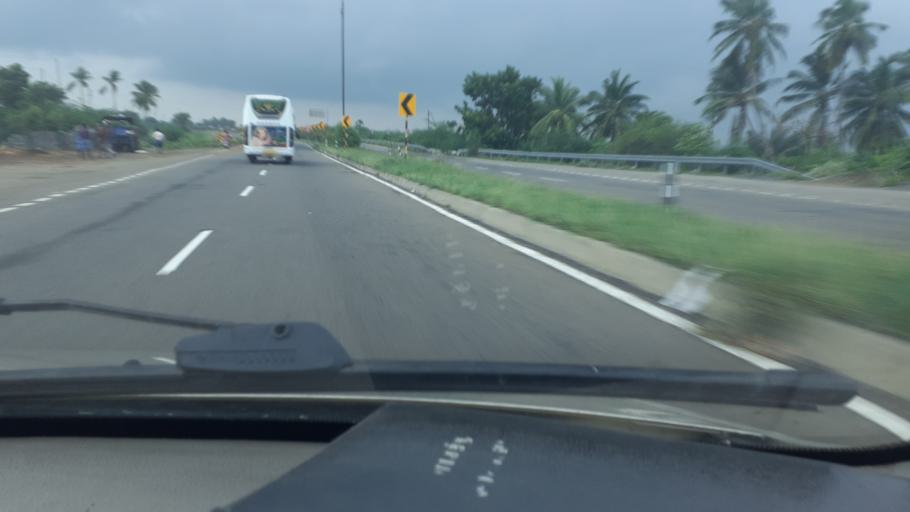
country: IN
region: Tamil Nadu
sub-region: Thoothukkudi
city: Kovilpatti
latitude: 9.1346
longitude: 77.8255
